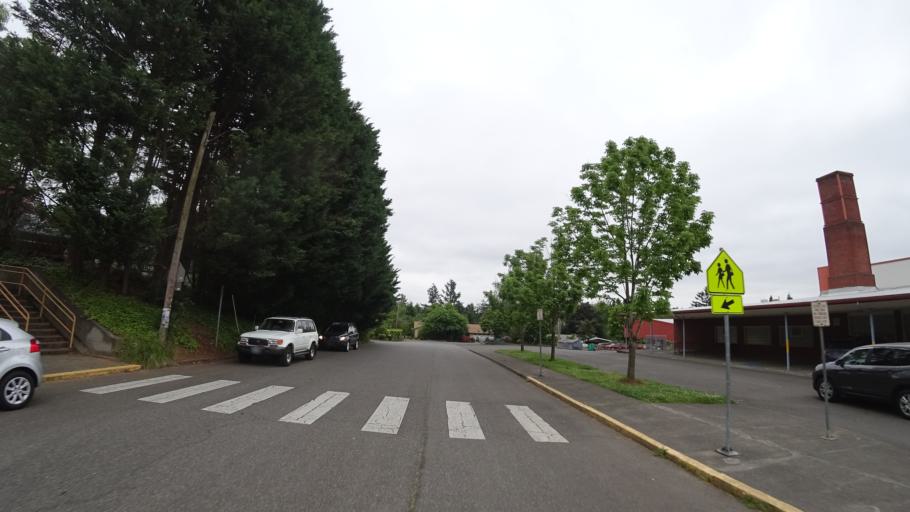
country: US
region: Oregon
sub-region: Multnomah County
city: Portland
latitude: 45.4822
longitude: -122.7009
